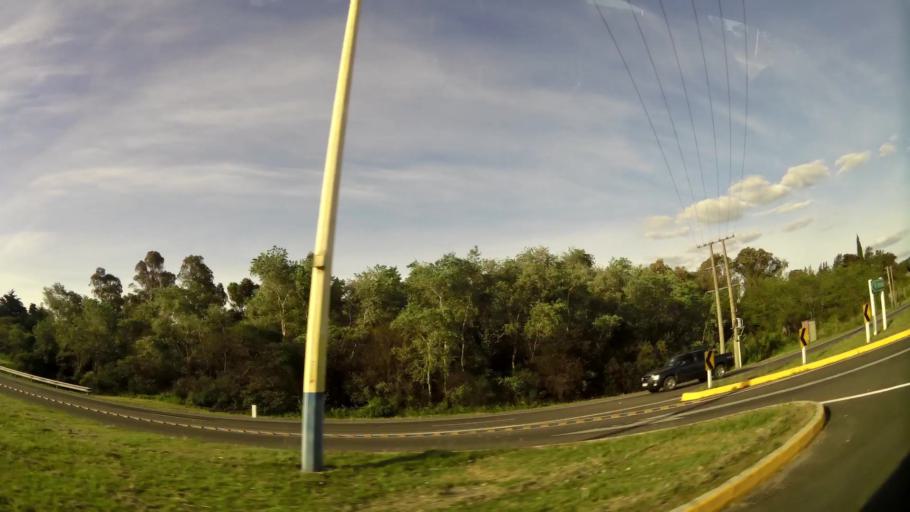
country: UY
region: Maldonado
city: Piriapolis
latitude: -34.7866
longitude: -55.3735
